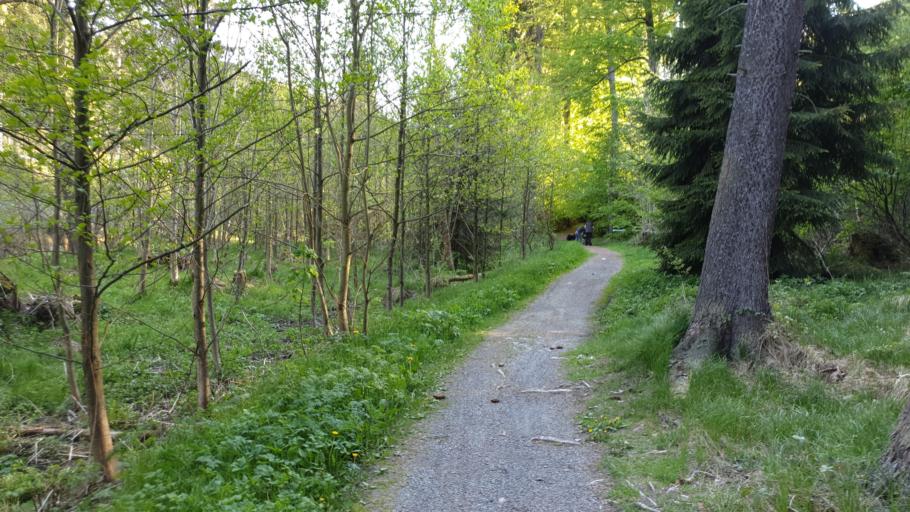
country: DE
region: Saxony
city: Johstadt
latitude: 50.5501
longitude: 13.1412
